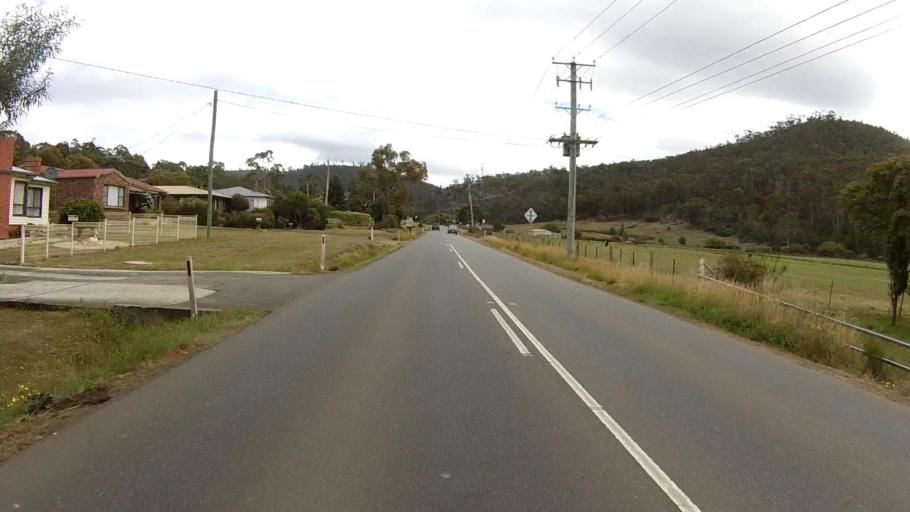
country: AU
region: Tasmania
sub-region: Clarence
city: Cambridge
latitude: -42.8394
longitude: 147.4247
